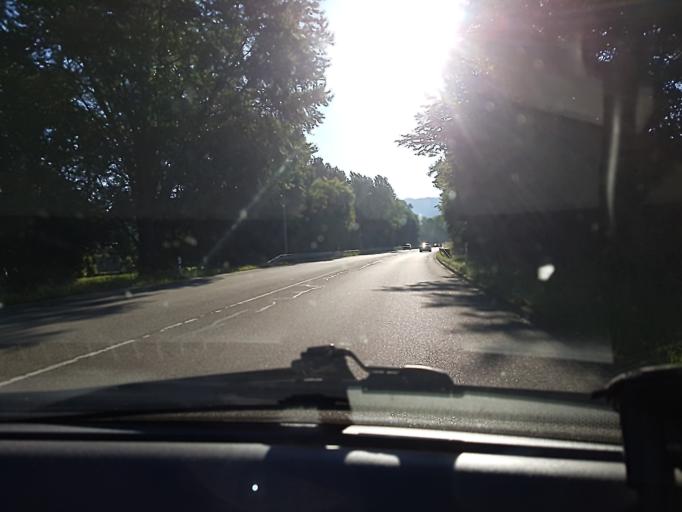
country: DE
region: Baden-Wuerttemberg
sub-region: Freiburg Region
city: Offenburg
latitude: 48.4601
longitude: 7.9461
